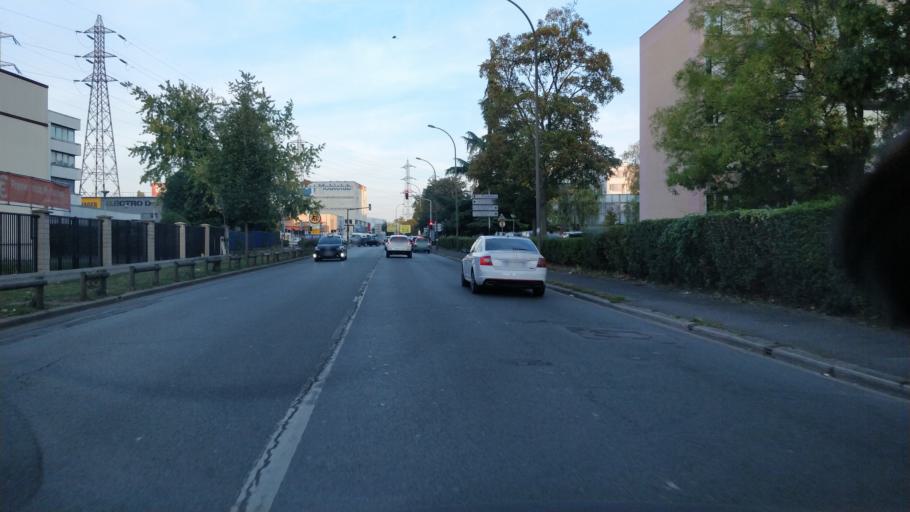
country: FR
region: Ile-de-France
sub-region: Departement de Seine-Saint-Denis
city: Villemomble
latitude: 48.8841
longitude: 2.4868
